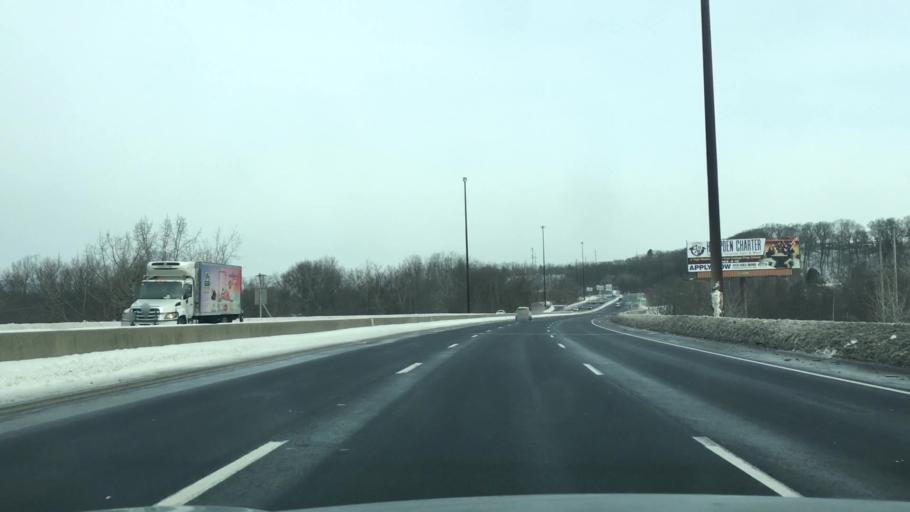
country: US
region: Massachusetts
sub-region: Hampden County
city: Chicopee
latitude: 42.1479
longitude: -72.6139
